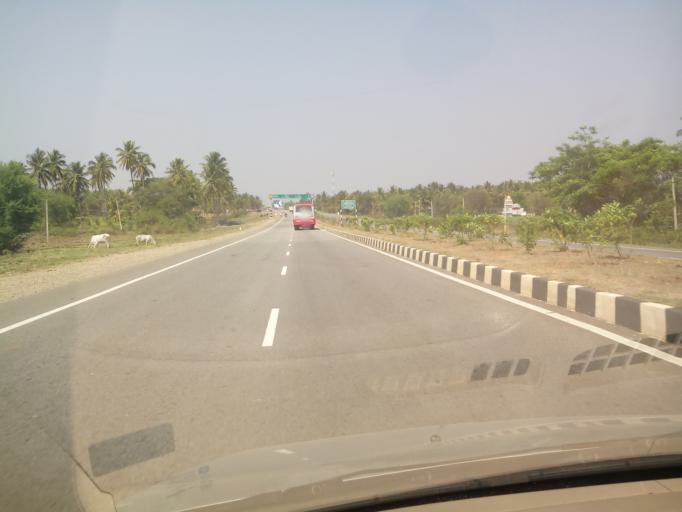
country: IN
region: Karnataka
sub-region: Hassan
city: Channarayapatna
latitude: 12.9085
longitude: 76.4340
